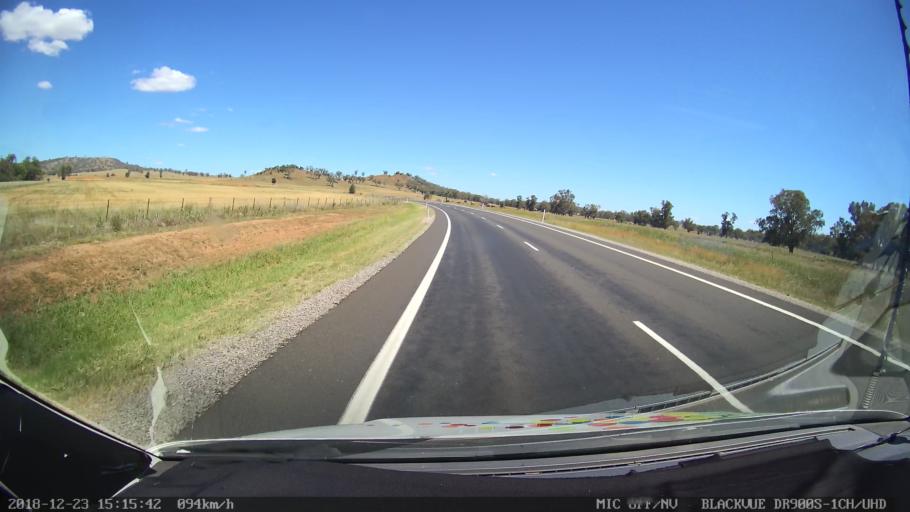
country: AU
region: New South Wales
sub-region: Tamworth Municipality
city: Manilla
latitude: -30.7896
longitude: 150.7440
